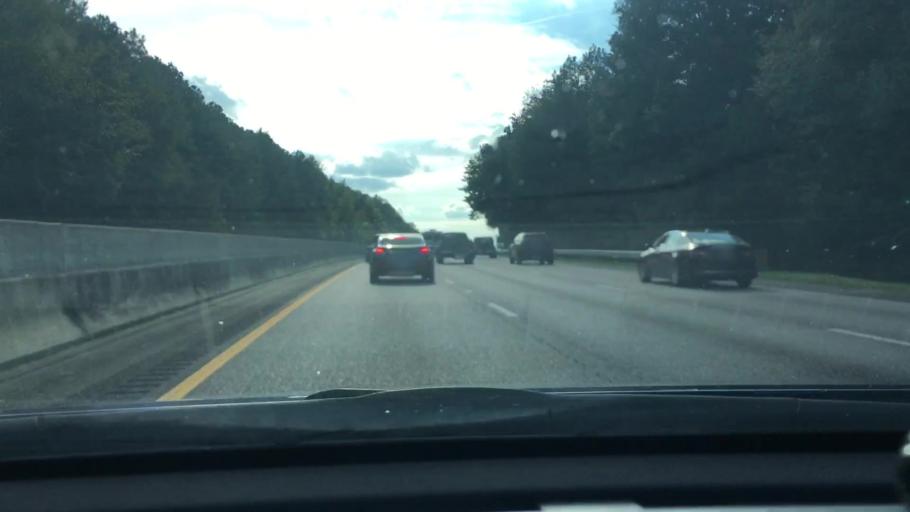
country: US
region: South Carolina
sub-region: Richland County
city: Columbia
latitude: 34.0574
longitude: -81.0528
